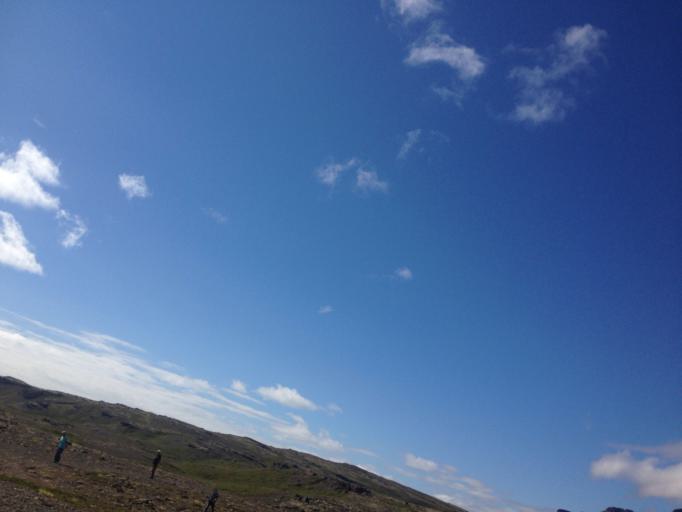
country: IS
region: West
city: Stykkisholmur
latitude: 64.8773
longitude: -22.7915
